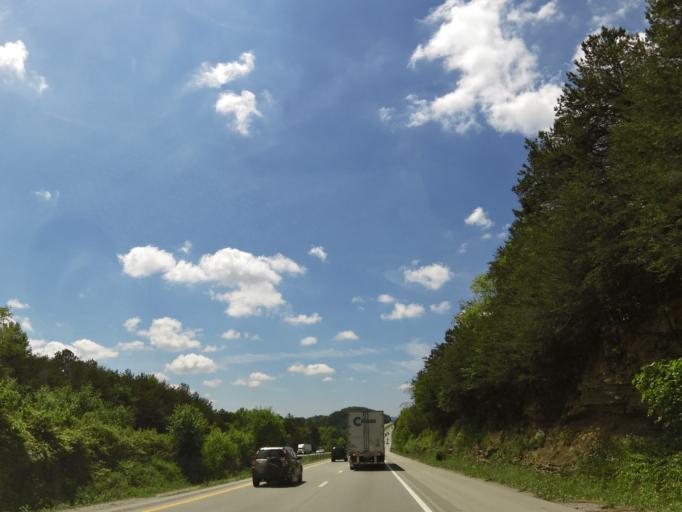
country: US
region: Kentucky
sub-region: Whitley County
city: Williamsburg
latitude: 36.8239
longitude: -84.1647
